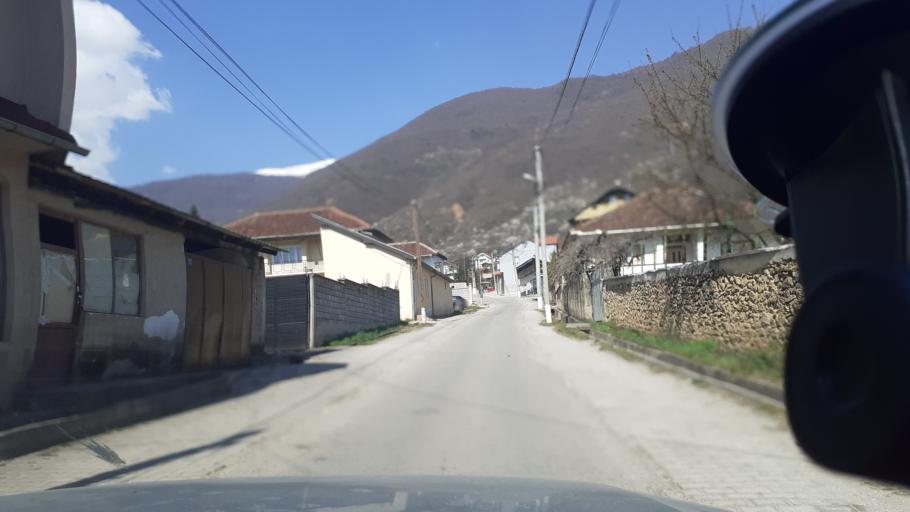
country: MK
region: Tearce
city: Slatino
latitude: 42.0703
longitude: 21.0440
